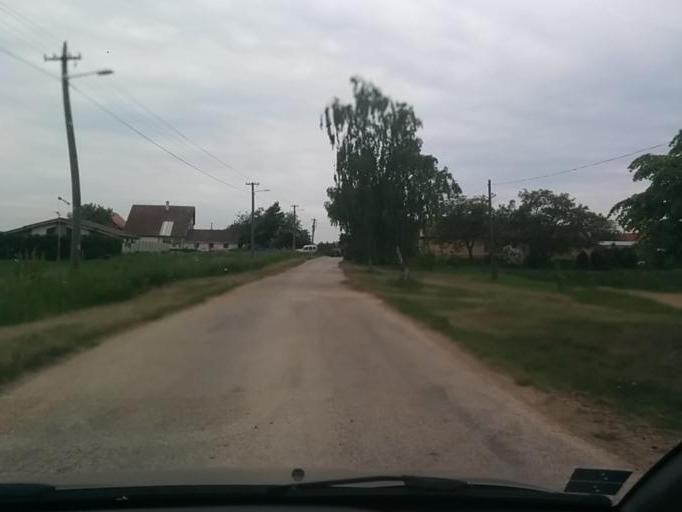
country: SK
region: Trnavsky
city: Sladkovicovo
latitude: 48.2612
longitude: 17.5808
